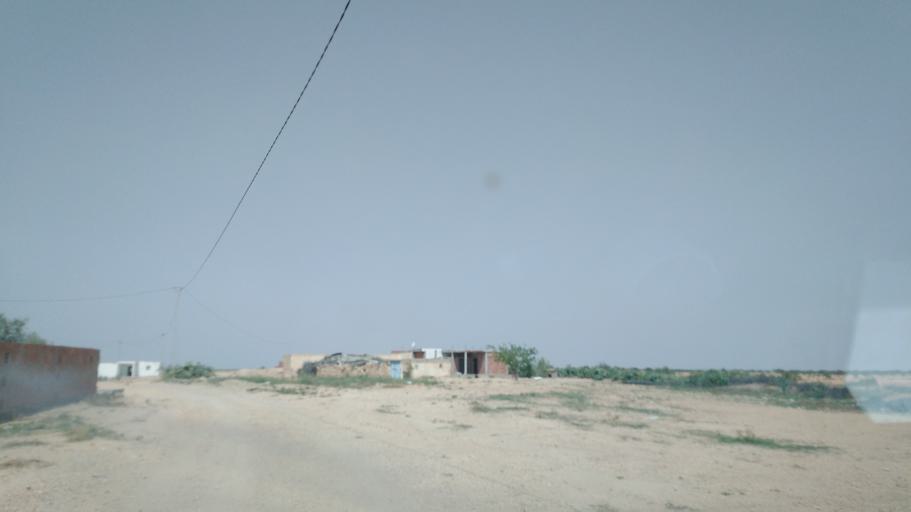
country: TN
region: Safaqis
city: Sfax
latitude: 34.6424
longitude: 10.5608
